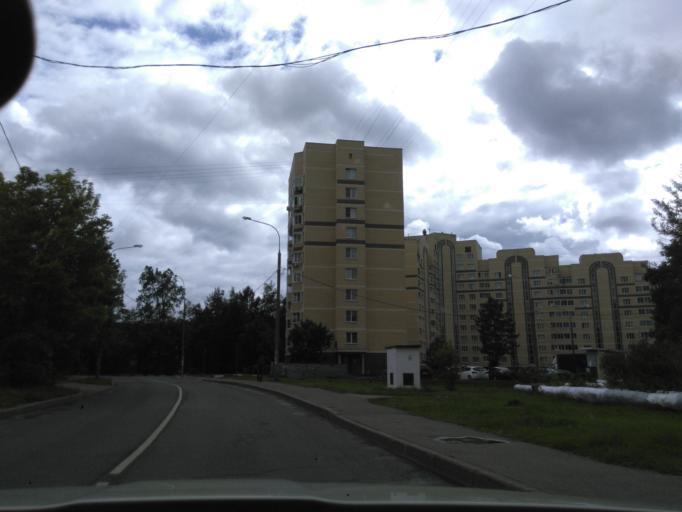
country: RU
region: Moskovskaya
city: Mendeleyevo
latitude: 56.0073
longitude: 37.2069
